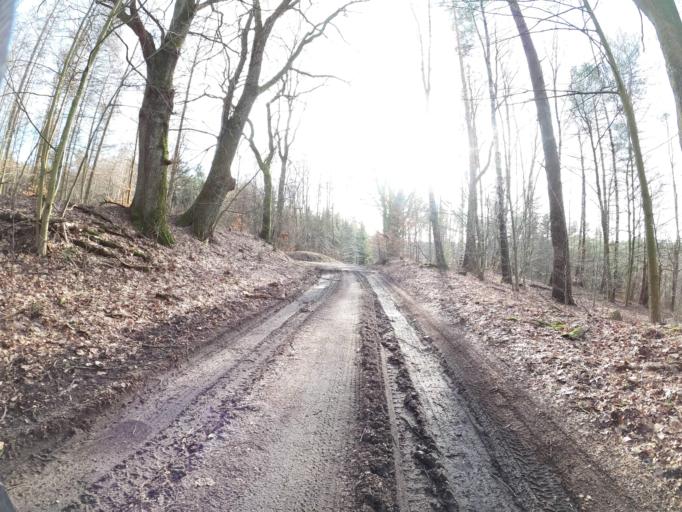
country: PL
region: West Pomeranian Voivodeship
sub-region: Powiat koszalinski
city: Polanow
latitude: 54.2285
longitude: 16.6398
